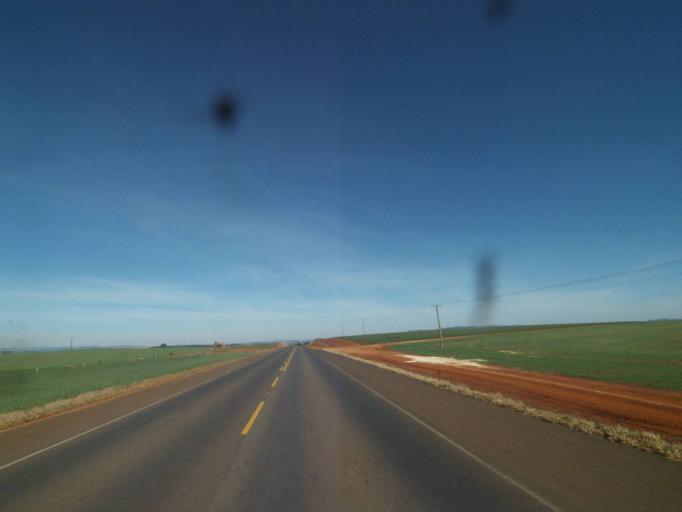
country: BR
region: Parana
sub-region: Tibagi
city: Tibagi
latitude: -24.4464
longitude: -50.4234
